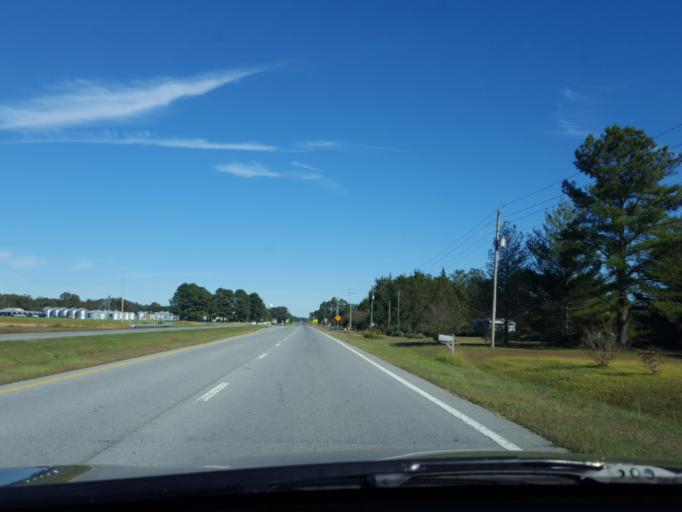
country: US
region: North Carolina
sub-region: Pitt County
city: Greenville
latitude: 35.6225
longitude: -77.2338
